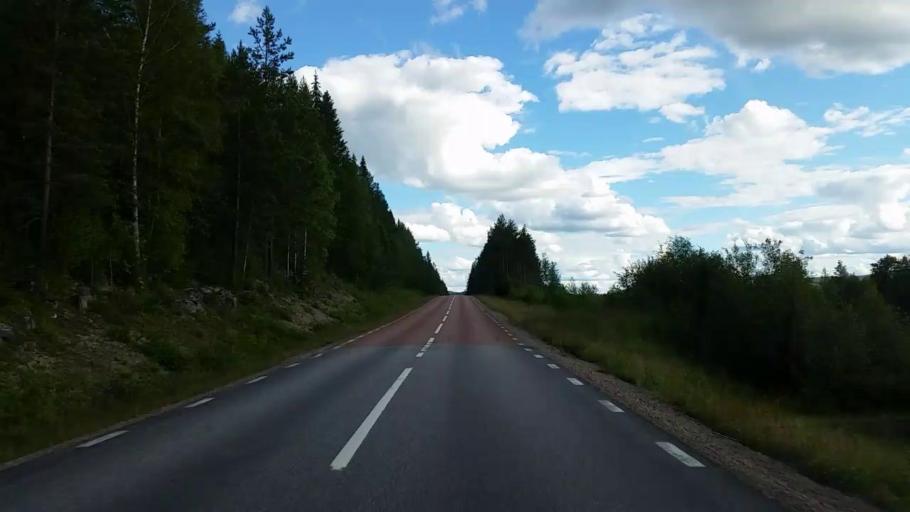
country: SE
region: Vaesternorrland
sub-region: Ange Kommun
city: Ange
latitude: 62.1486
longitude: 15.6837
